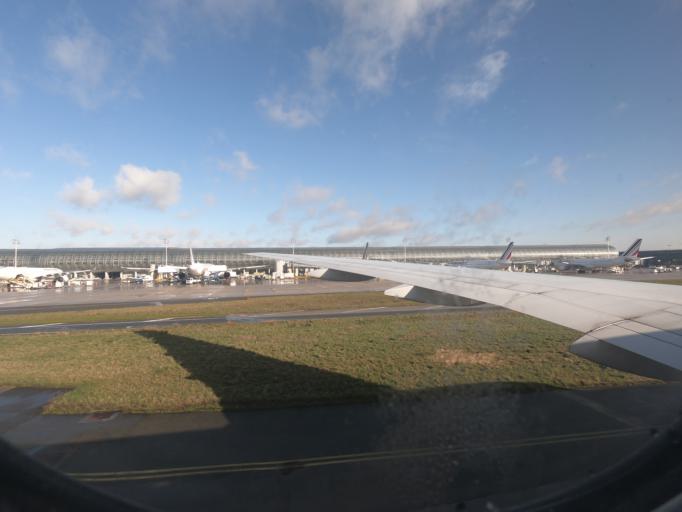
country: FR
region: Ile-de-France
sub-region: Departement de Seine-et-Marne
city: Mitry-Mory
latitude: 48.9999
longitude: 2.5790
